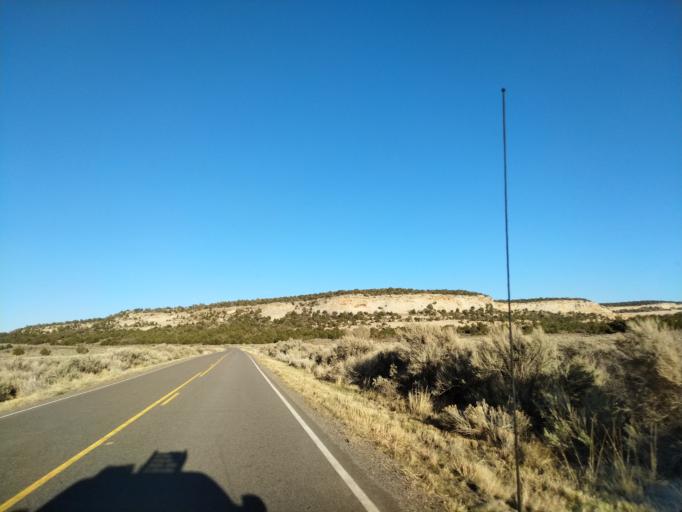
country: US
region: Colorado
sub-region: Mesa County
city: Fruita
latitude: 38.9830
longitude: -108.8004
